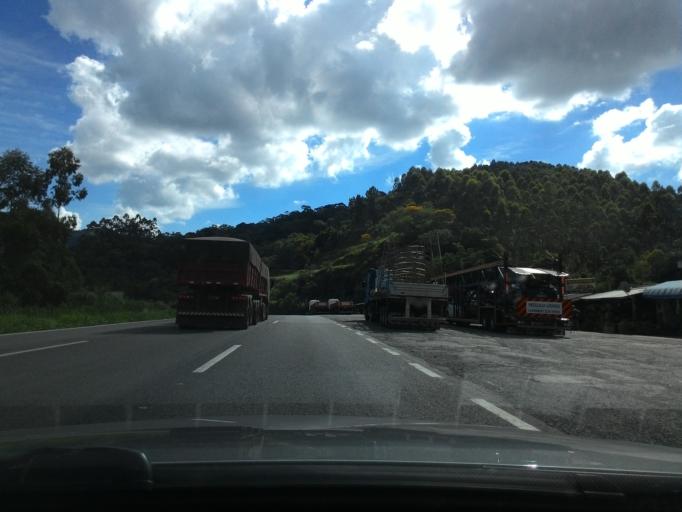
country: BR
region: Sao Paulo
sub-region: Cajati
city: Cajati
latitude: -24.7941
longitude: -48.2122
